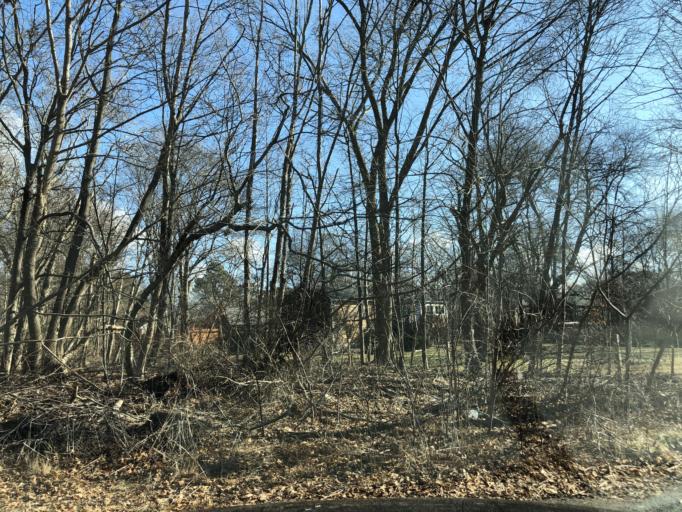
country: US
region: Massachusetts
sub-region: Plymouth County
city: Brockton
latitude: 42.1134
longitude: -71.0152
